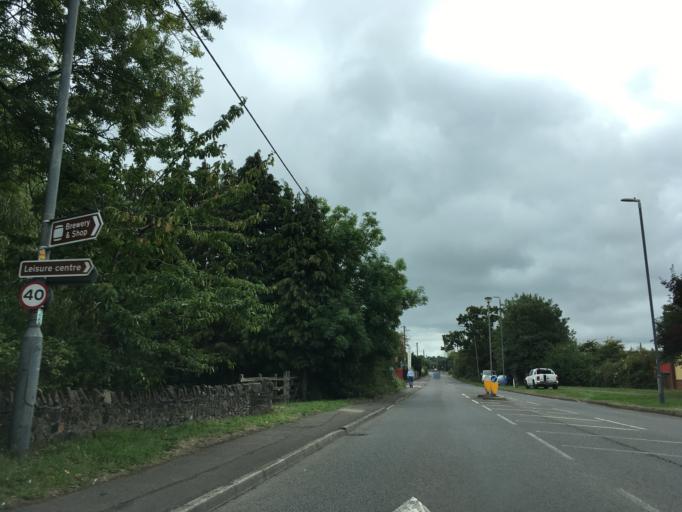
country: GB
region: England
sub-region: South Gloucestershire
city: Bitton
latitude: 51.4501
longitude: -2.4632
